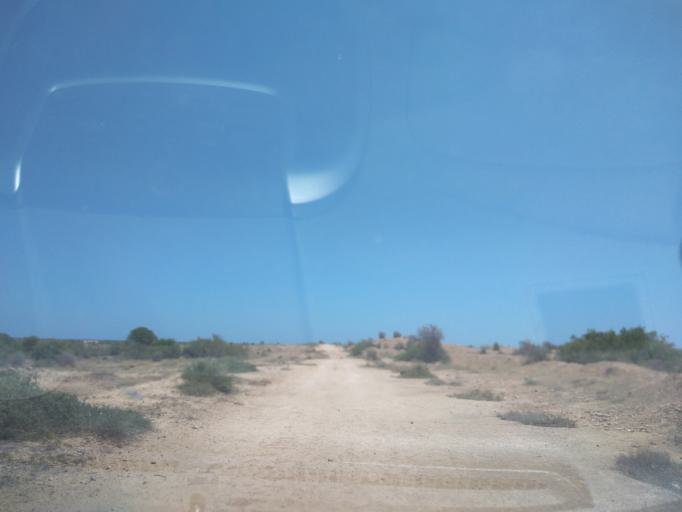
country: TN
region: Susah
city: Harqalah
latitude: 36.1710
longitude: 10.4431
